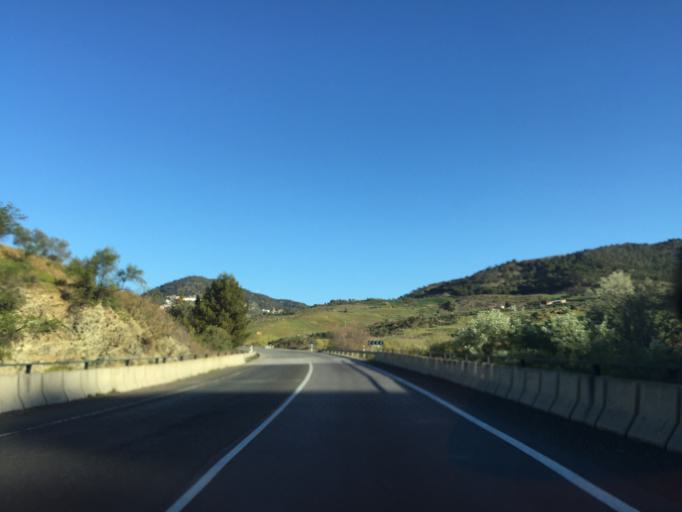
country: ES
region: Andalusia
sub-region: Provincia de Malaga
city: Carratraca
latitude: 36.8372
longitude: -4.8082
